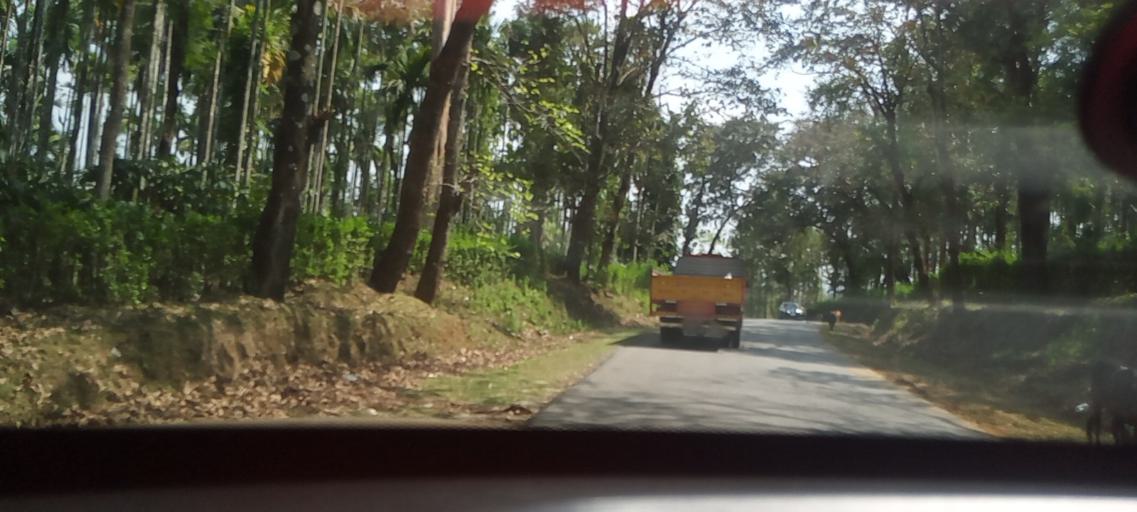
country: IN
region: Karnataka
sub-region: Chikmagalur
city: Mudigere
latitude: 13.3210
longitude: 75.5666
